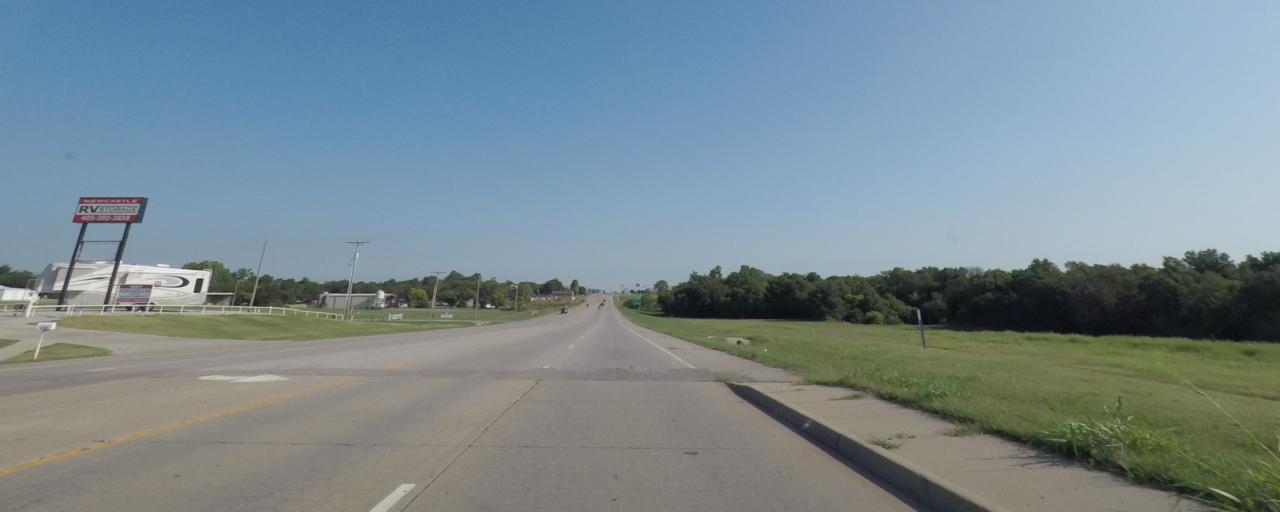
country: US
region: Oklahoma
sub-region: McClain County
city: Newcastle
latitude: 35.2646
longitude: -97.6001
